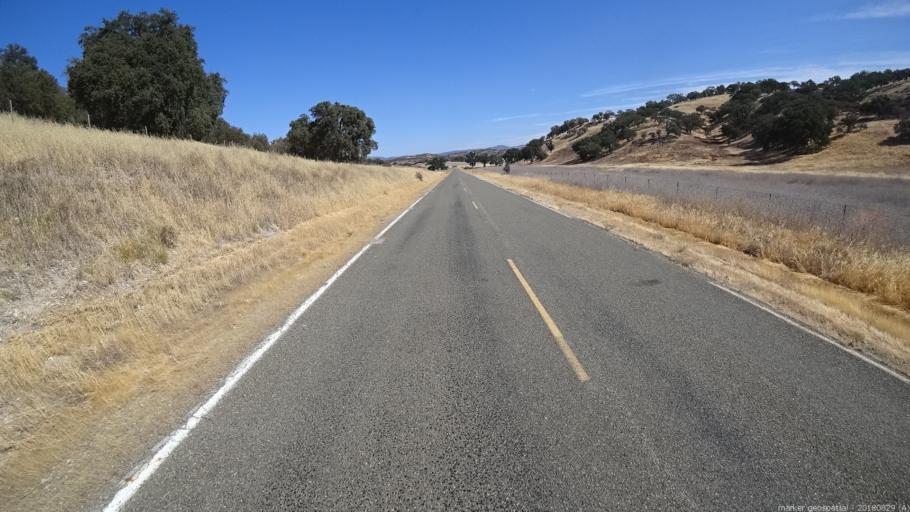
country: US
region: California
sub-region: San Luis Obispo County
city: Lake Nacimiento
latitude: 35.8790
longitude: -121.0661
